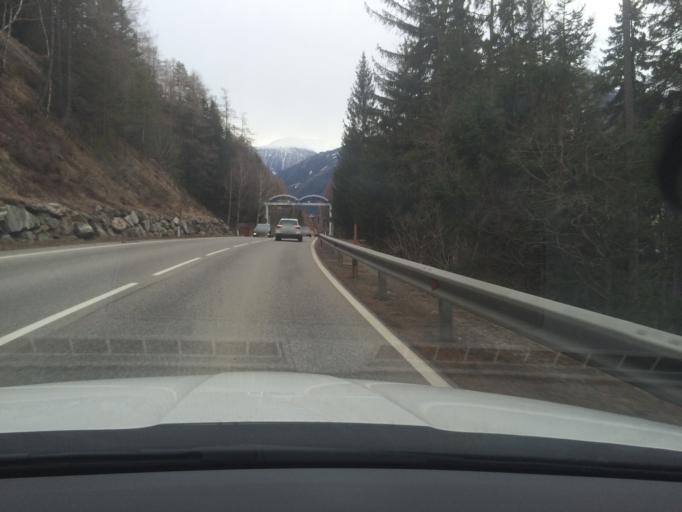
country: AT
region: Tyrol
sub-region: Politischer Bezirk Lienz
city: Matrei in Osttirol
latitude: 47.0126
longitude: 12.5392
